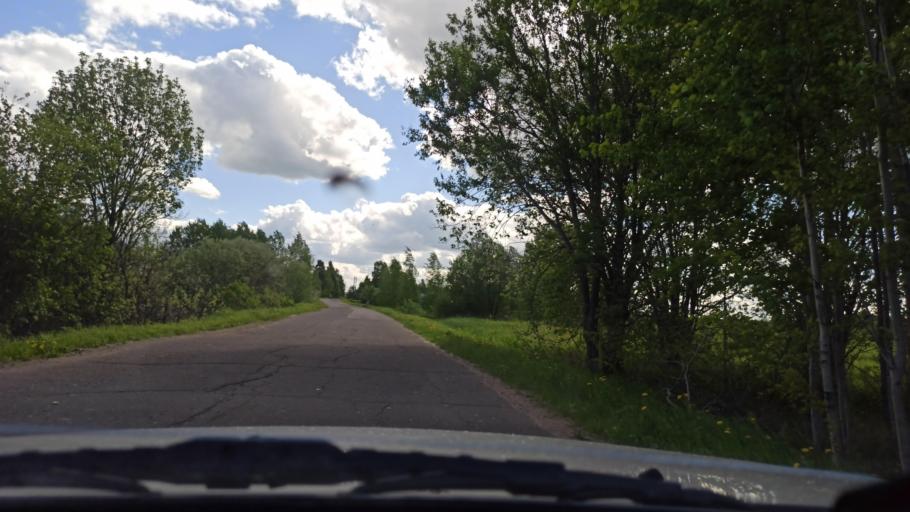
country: RU
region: Vologda
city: Molochnoye
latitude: 59.3807
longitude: 39.7200
